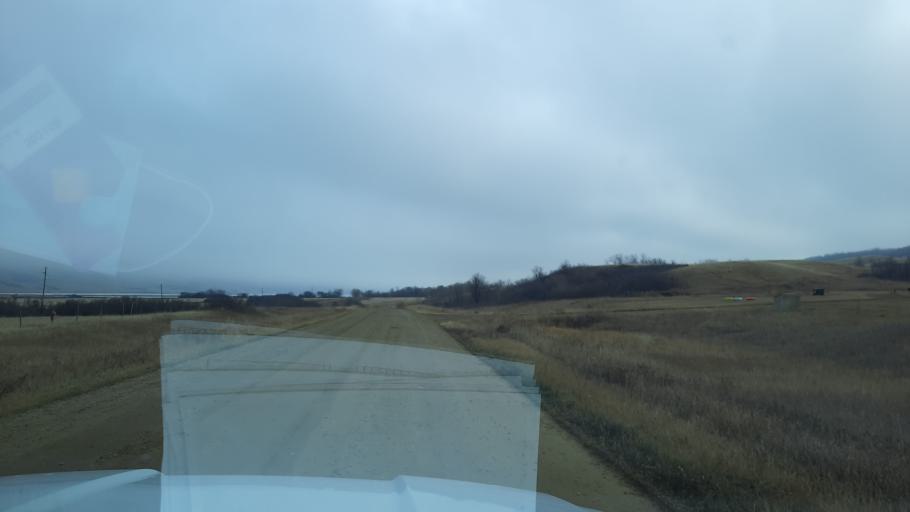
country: CA
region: Saskatchewan
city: White City
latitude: 50.7811
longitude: -104.1425
